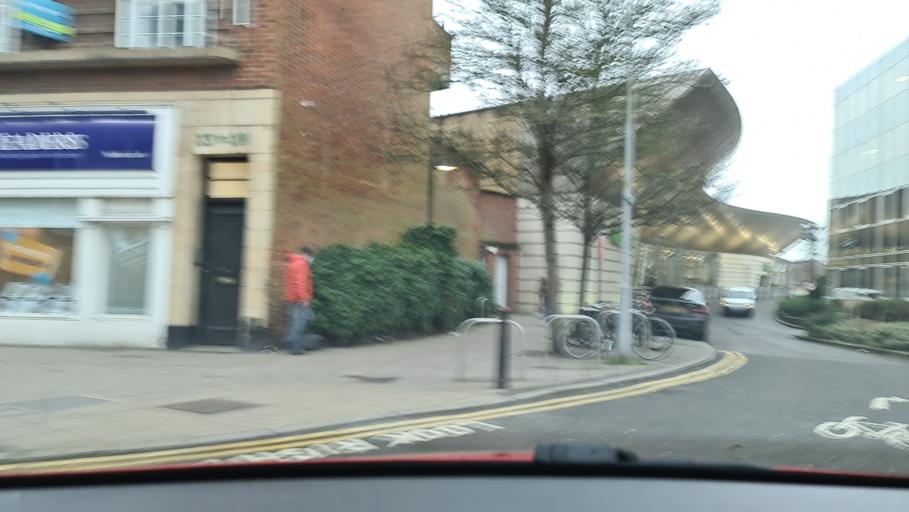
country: GB
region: England
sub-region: Greater London
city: Surbiton
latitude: 51.3941
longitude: -0.3043
